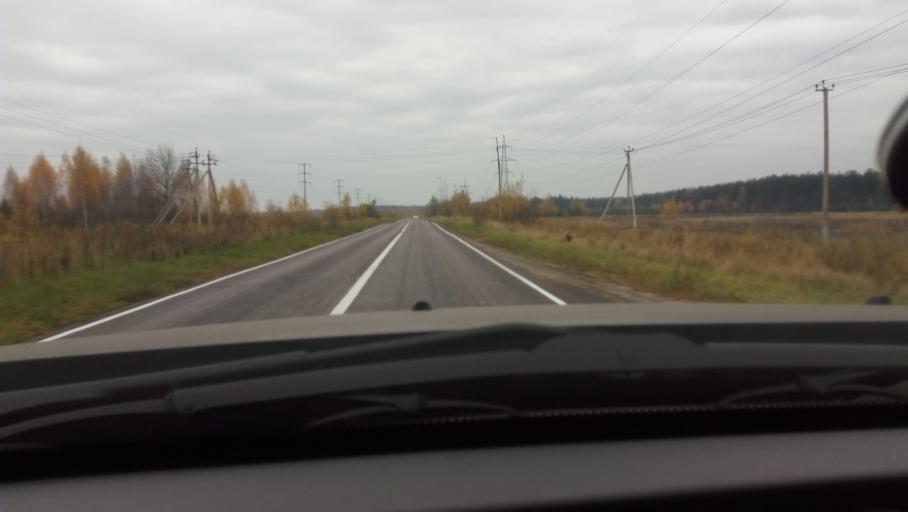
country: RU
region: Moskovskaya
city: Avsyunino
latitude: 55.6037
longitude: 39.1826
